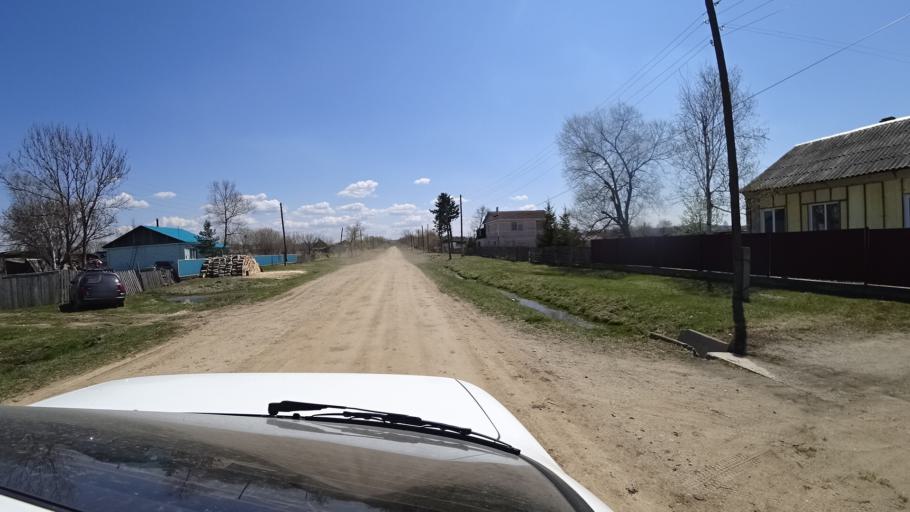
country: RU
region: Primorskiy
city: Dal'nerechensk
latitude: 45.8031
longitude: 133.7645
